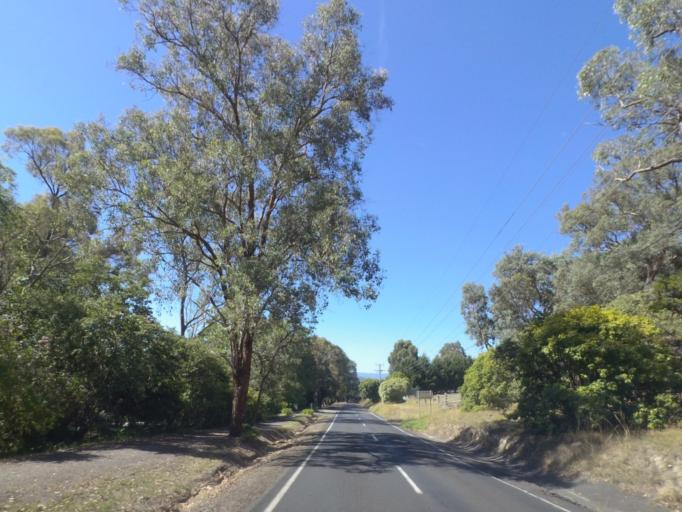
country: AU
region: Victoria
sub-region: Maroondah
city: Croydon Hills
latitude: -37.7484
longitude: 145.2718
